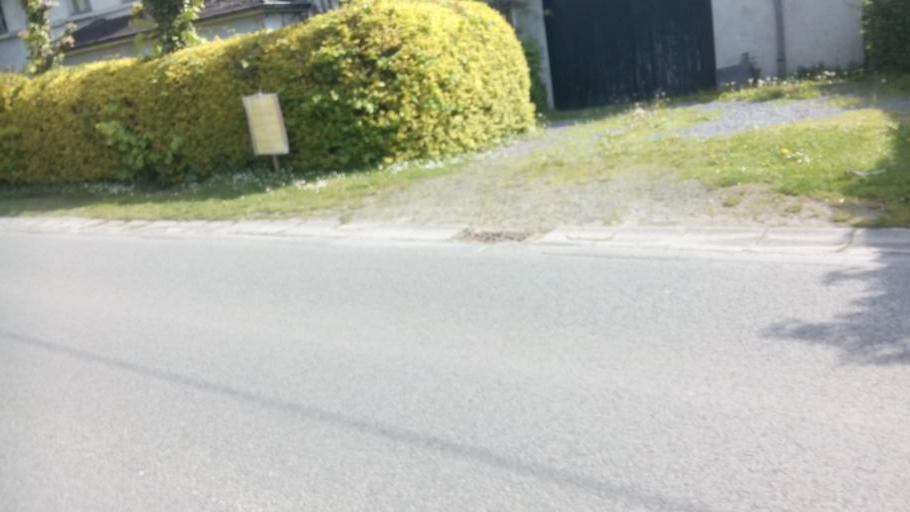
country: BE
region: Flanders
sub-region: Provincie Oost-Vlaanderen
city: Lovendegem
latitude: 51.0731
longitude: 3.5787
